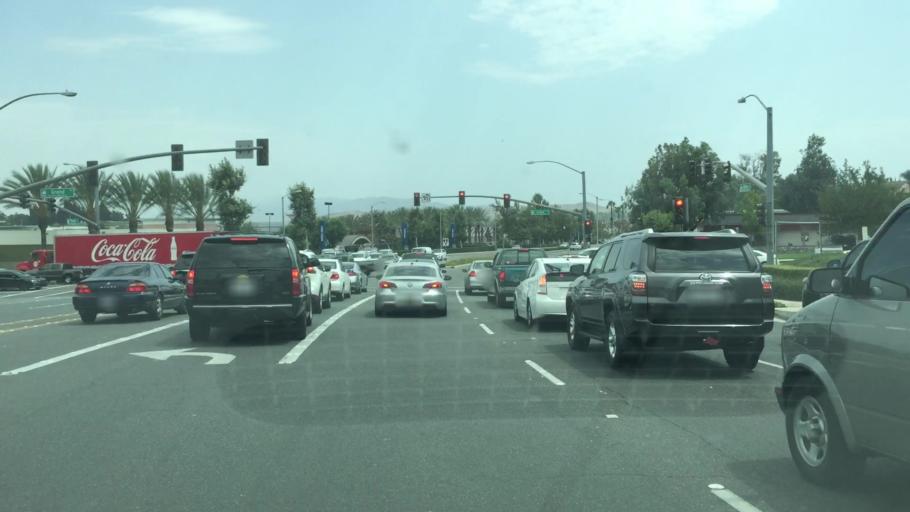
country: US
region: California
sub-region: San Bernardino County
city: Chino Hills
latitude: 34.0029
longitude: -117.7332
